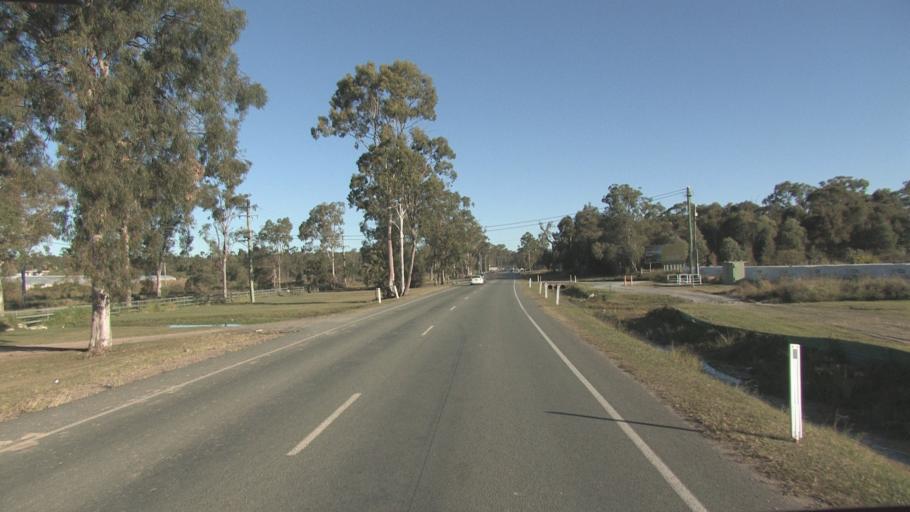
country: AU
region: Queensland
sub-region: Logan
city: Logan Reserve
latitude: -27.7147
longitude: 153.0927
